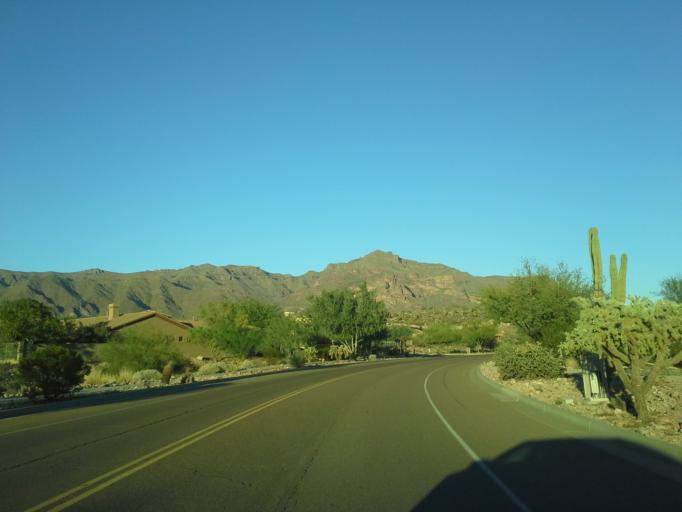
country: US
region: Arizona
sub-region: Pinal County
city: Apache Junction
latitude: 33.3804
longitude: -111.4552
